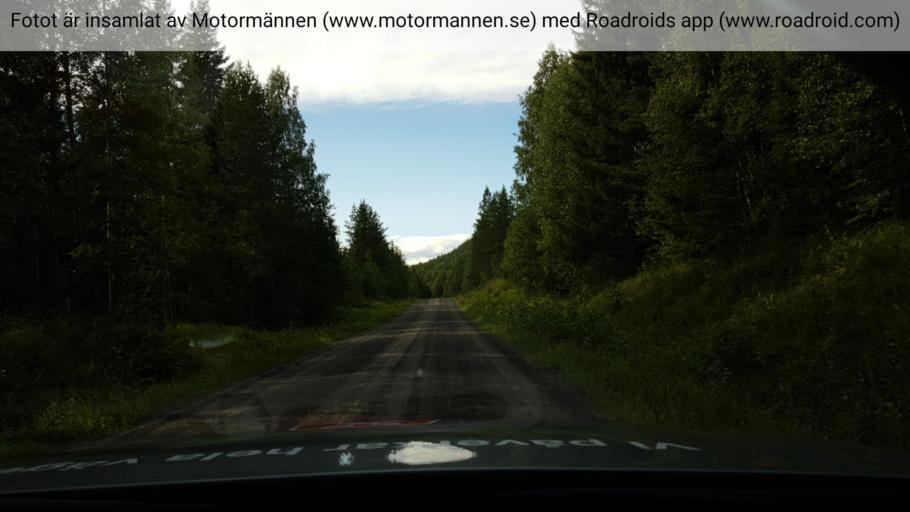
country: SE
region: Jaemtland
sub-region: Braecke Kommun
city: Braecke
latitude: 63.2085
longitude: 15.3961
